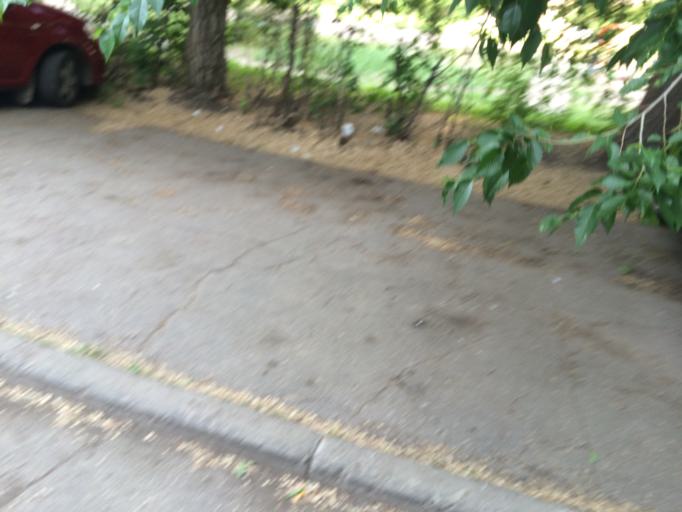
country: RU
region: Chelyabinsk
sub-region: Gorod Magnitogorsk
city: Magnitogorsk
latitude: 53.4040
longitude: 58.9835
